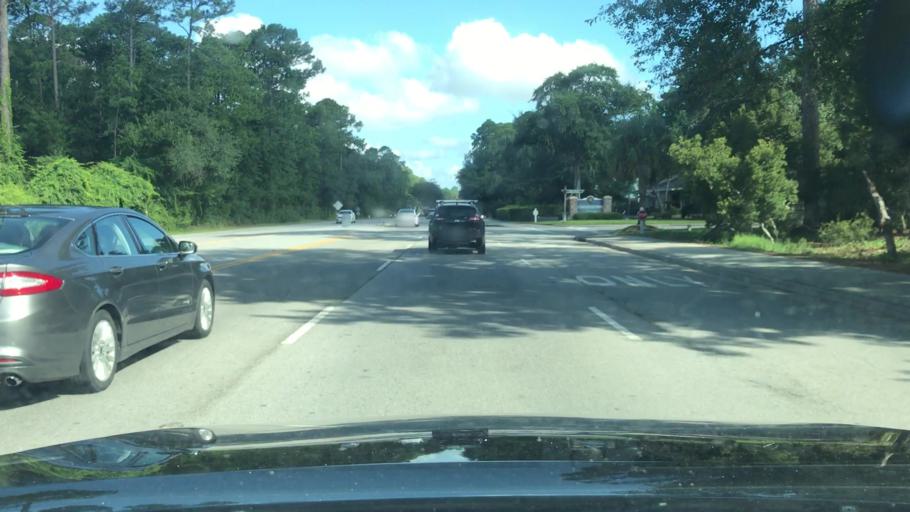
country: US
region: South Carolina
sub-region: Beaufort County
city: Hilton Head Island
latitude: 32.1616
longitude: -80.7676
